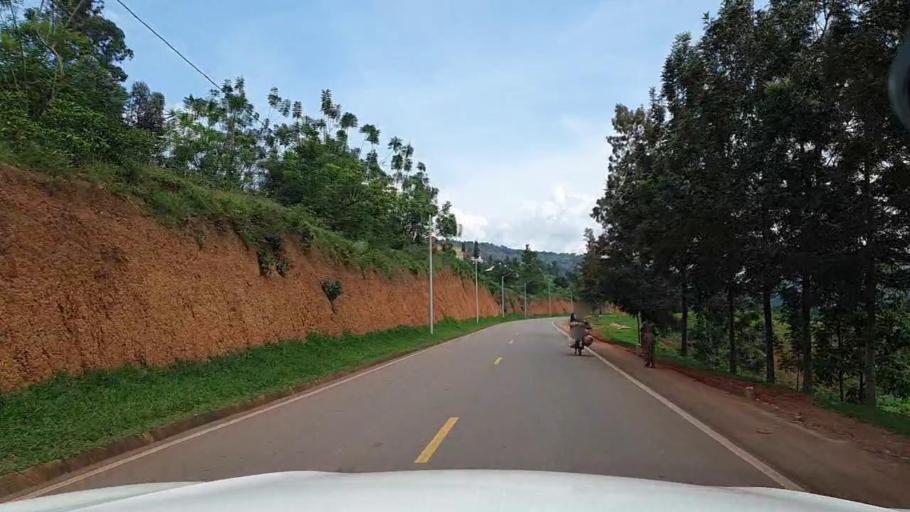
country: RW
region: Kigali
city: Kigali
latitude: -1.8739
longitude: 30.0824
